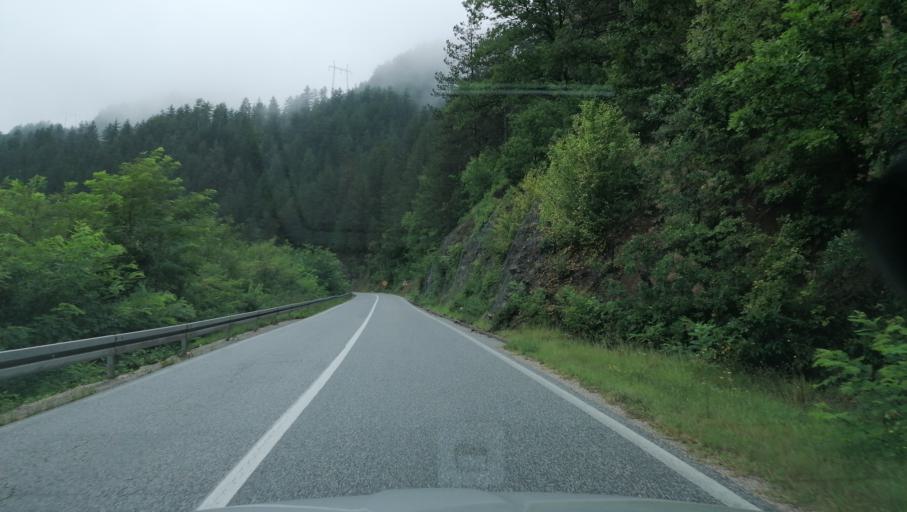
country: BA
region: Republika Srpska
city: Visegrad
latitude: 43.7834
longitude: 19.3478
